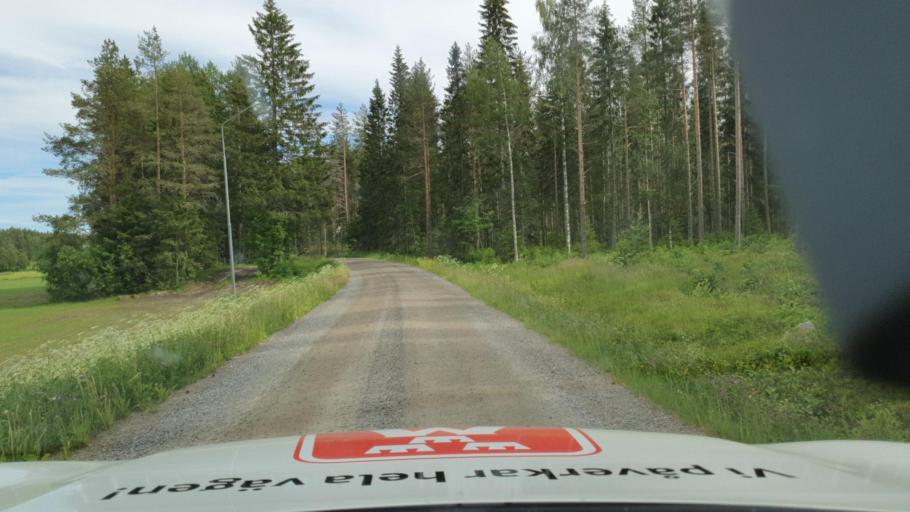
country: SE
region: Vaesterbotten
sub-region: Robertsfors Kommun
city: Robertsfors
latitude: 64.3747
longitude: 21.0397
